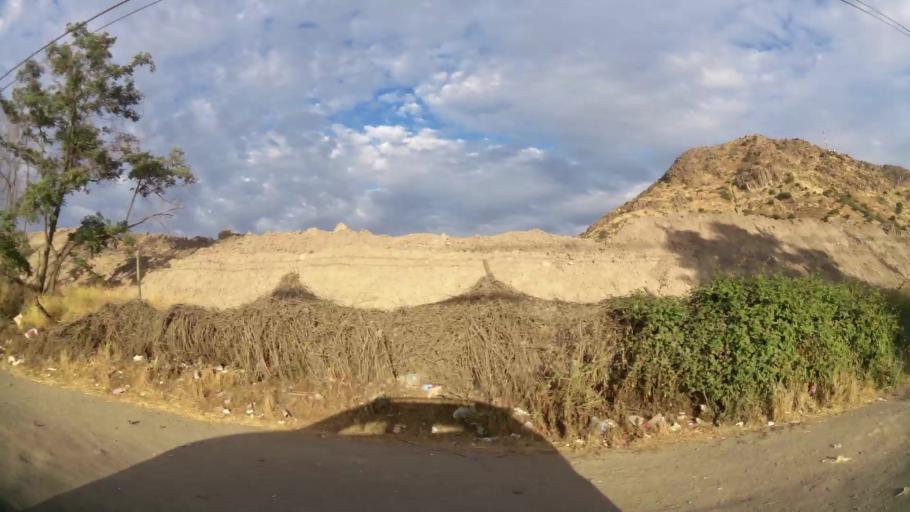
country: CL
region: Santiago Metropolitan
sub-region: Provincia de Maipo
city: San Bernardo
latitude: -33.6220
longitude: -70.6810
